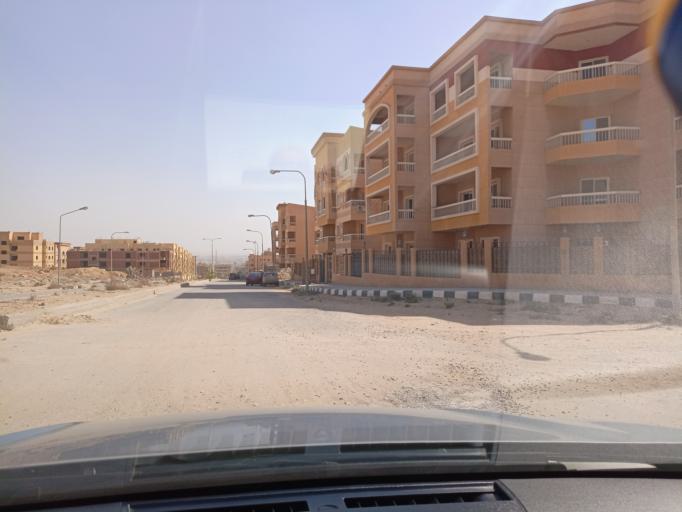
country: EG
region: Muhafazat al Qalyubiyah
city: Al Khankah
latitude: 30.2210
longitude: 31.4419
